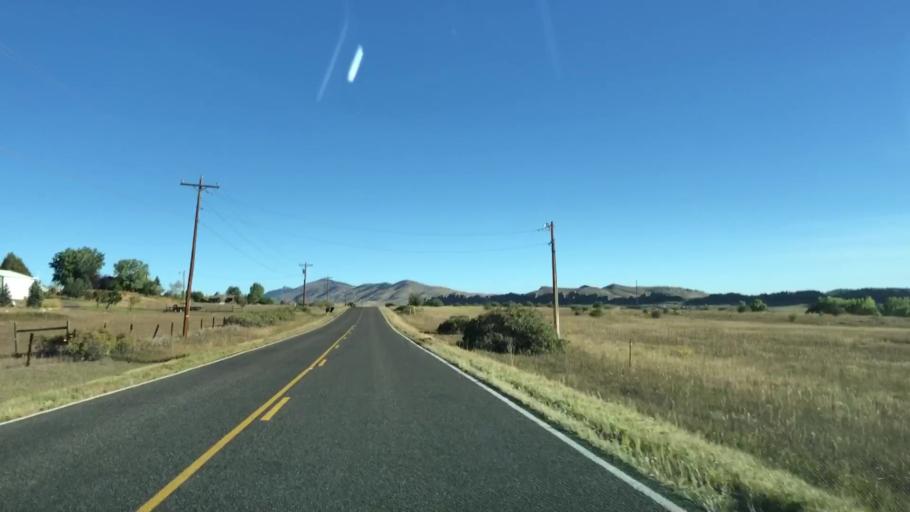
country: US
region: Colorado
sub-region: Larimer County
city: Loveland
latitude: 40.3982
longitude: -105.1684
